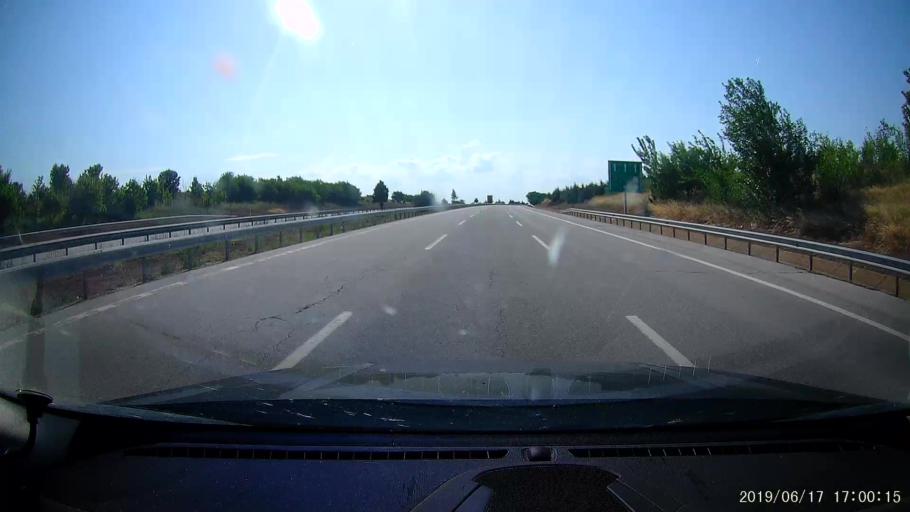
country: TR
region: Edirne
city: Haskoy
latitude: 41.6195
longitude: 26.8363
